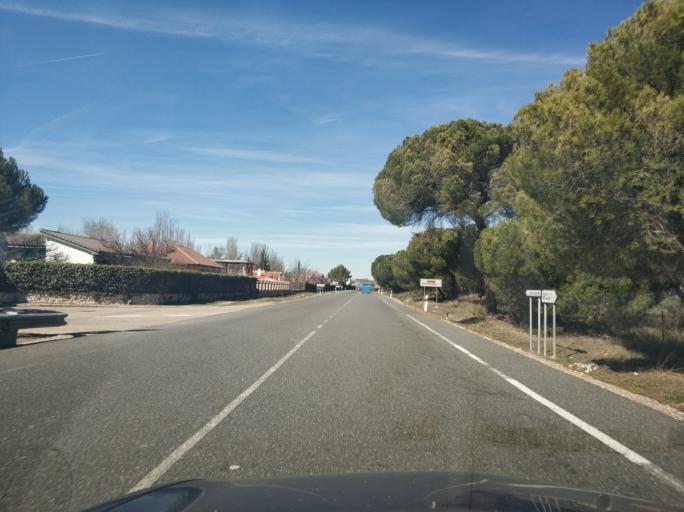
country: ES
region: Castille and Leon
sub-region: Provincia de Valladolid
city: Viana de Cega
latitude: 41.5446
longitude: -4.7819
